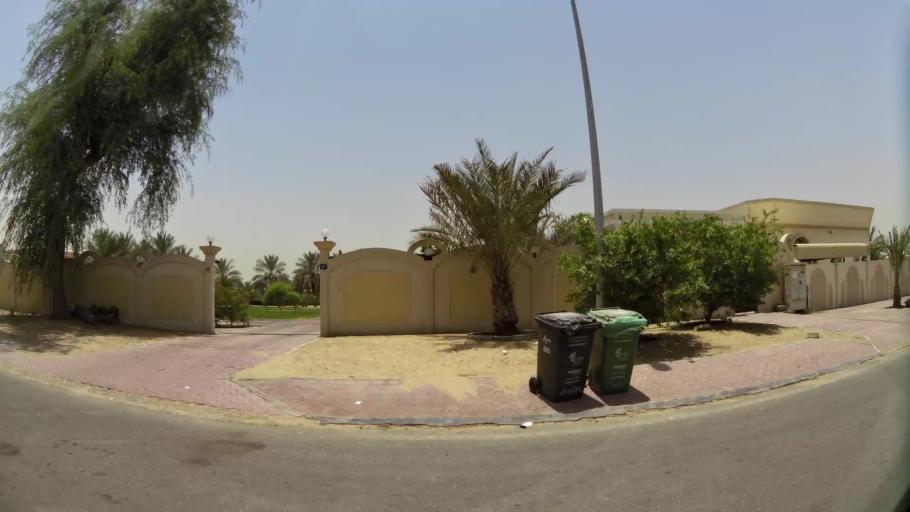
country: AE
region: Ash Shariqah
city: Sharjah
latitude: 25.2479
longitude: 55.4559
